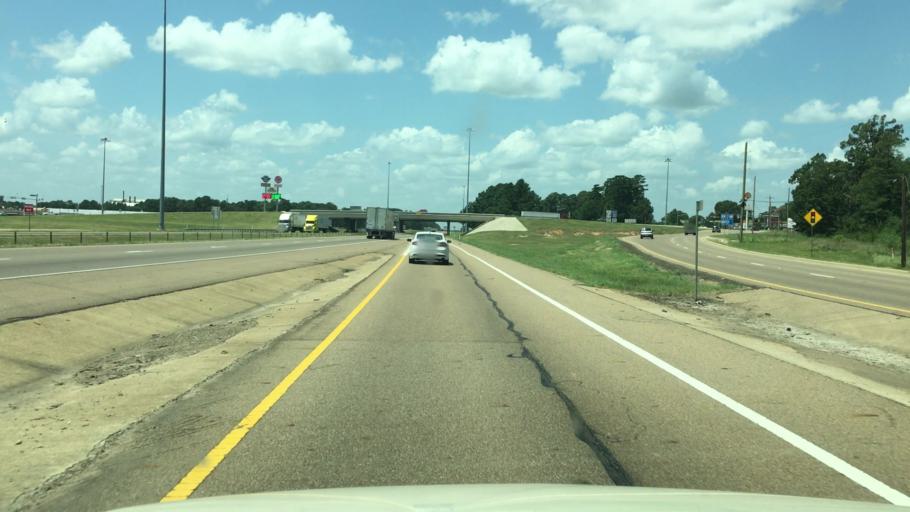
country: US
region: Texas
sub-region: Bowie County
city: Nash
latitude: 33.4539
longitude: -94.1269
